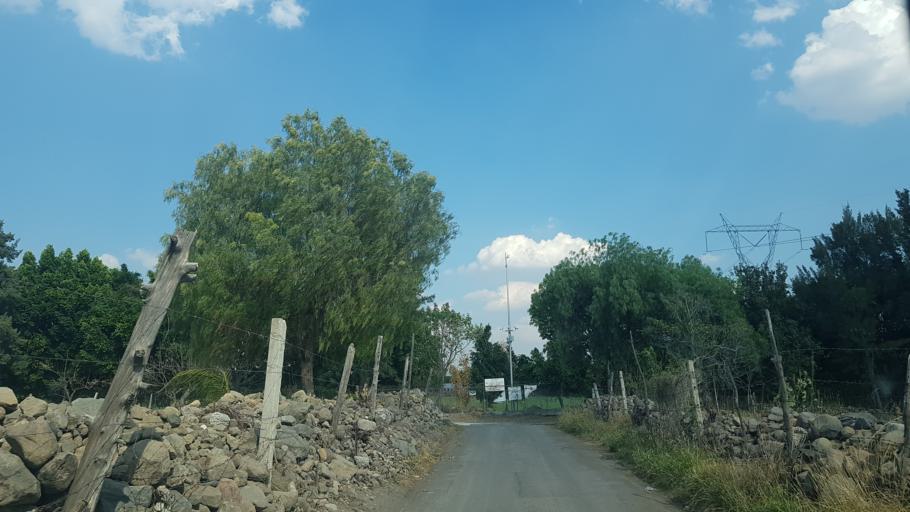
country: MX
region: Puebla
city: Atlixco
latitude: 18.8795
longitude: -98.4843
